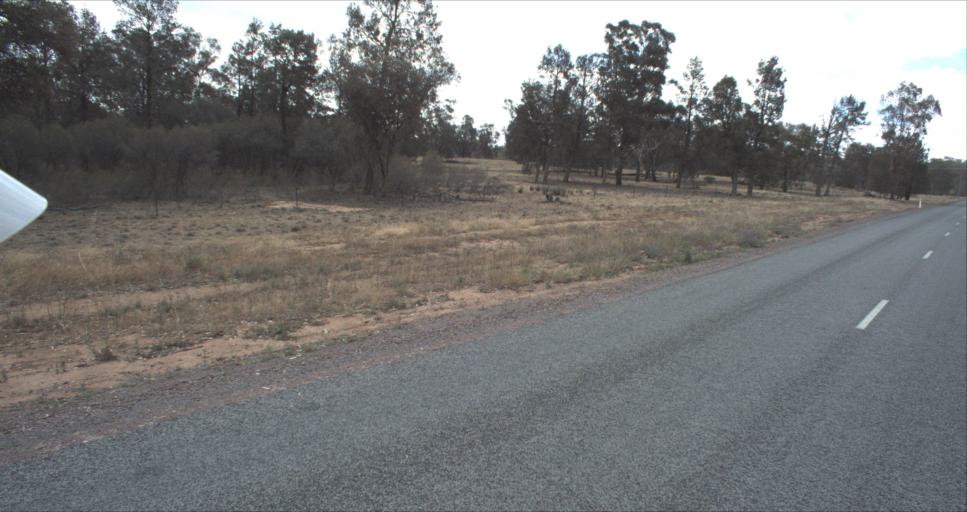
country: AU
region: New South Wales
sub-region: Leeton
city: Leeton
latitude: -34.6464
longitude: 146.3521
